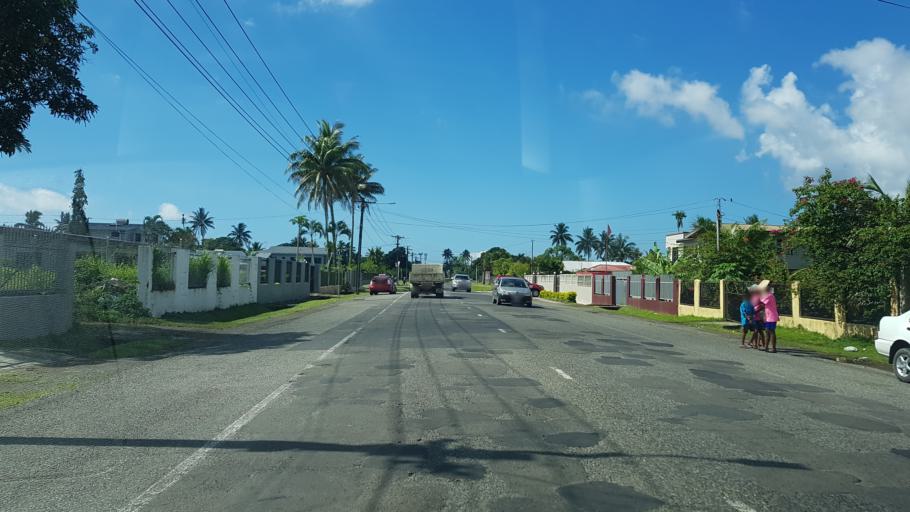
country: FJ
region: Central
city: Suva
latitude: -18.1307
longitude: 178.4592
